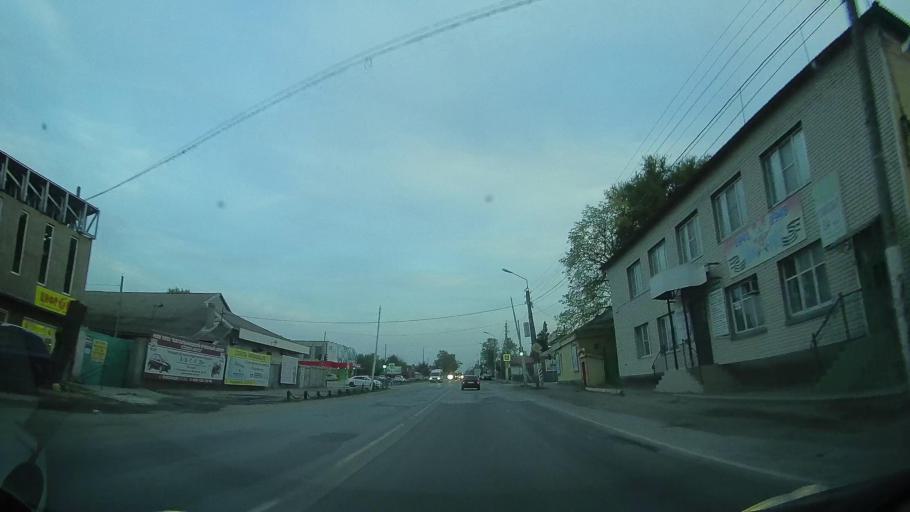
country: RU
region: Rostov
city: Kagal'nitskaya
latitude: 46.8820
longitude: 40.1492
